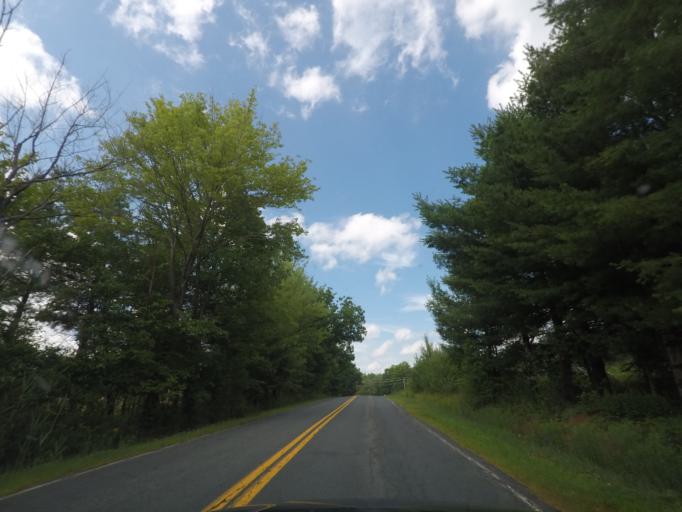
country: US
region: New York
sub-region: Rensselaer County
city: Averill Park
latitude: 42.6223
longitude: -73.5447
